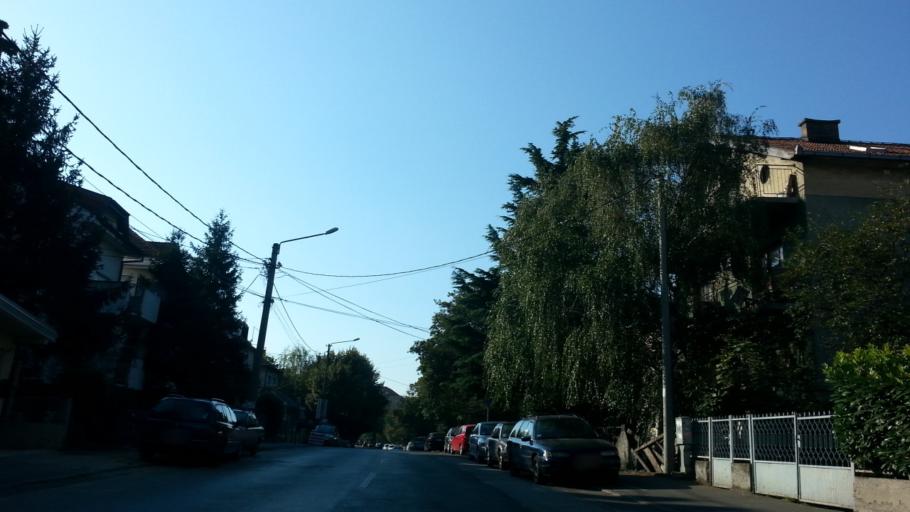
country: RS
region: Central Serbia
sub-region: Belgrade
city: Cukarica
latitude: 44.7620
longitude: 20.4189
